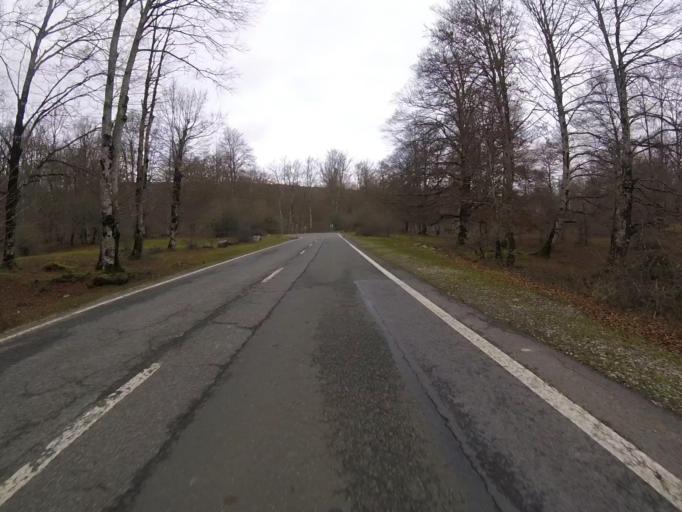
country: ES
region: Navarre
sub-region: Provincia de Navarra
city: Olazagutia
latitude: 42.8554
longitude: -2.1698
